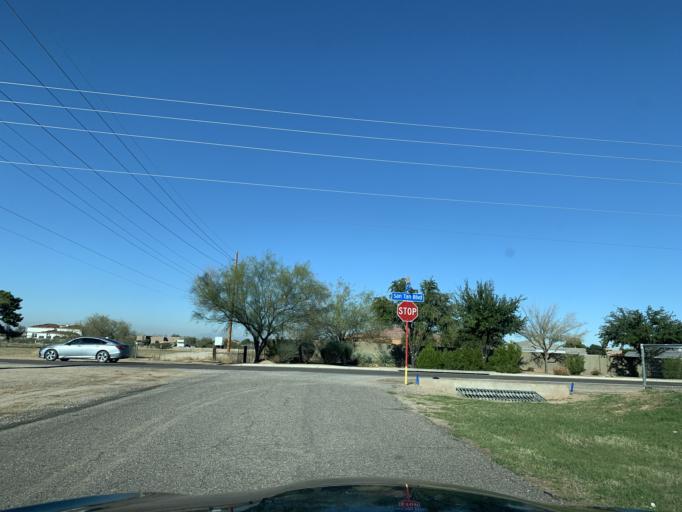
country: US
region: Arizona
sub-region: Maricopa County
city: Queen Creek
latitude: 33.2117
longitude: -111.7118
